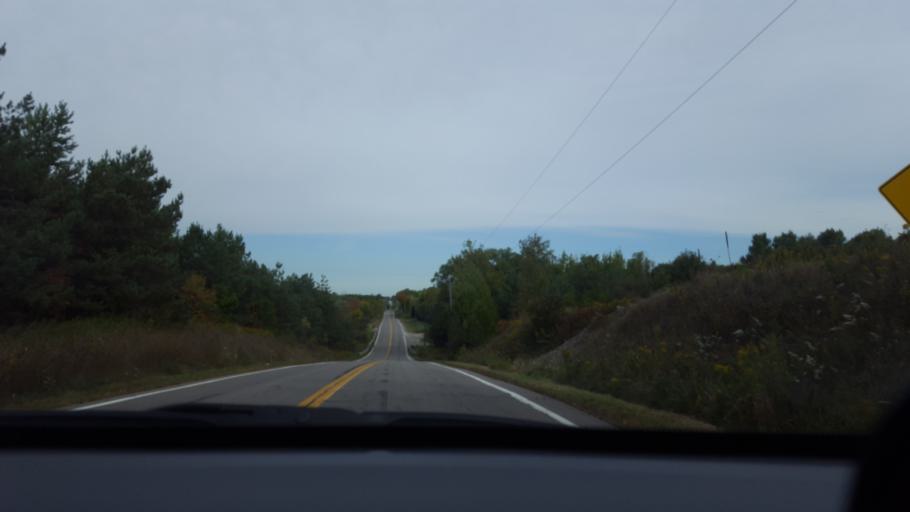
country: CA
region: Ontario
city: Newmarket
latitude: 43.9942
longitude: -79.5458
